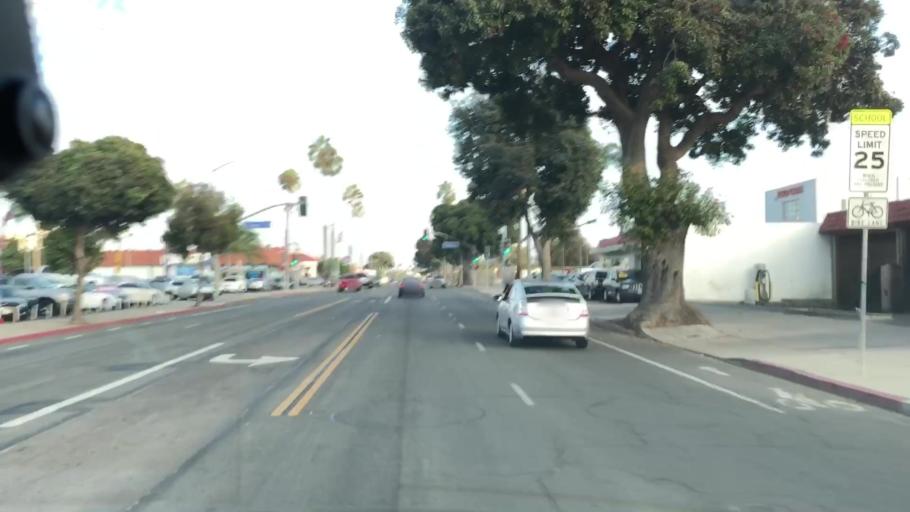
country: US
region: California
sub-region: Ventura County
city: Ventura
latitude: 34.2731
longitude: -119.2639
